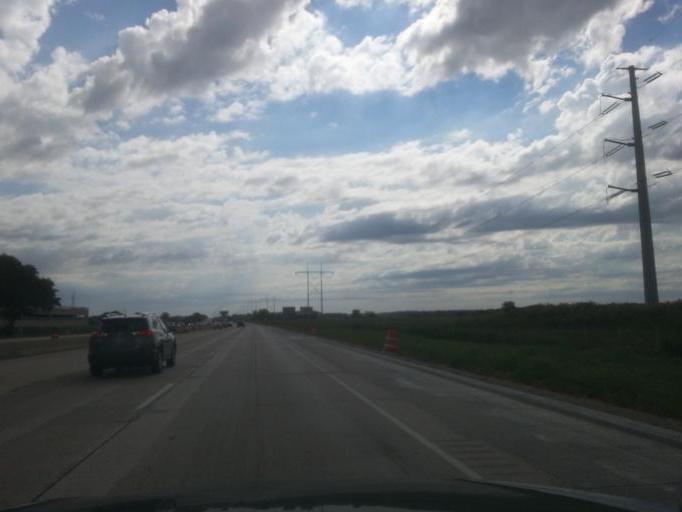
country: US
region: Wisconsin
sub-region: Dane County
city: Monona
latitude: 43.0437
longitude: -89.3437
